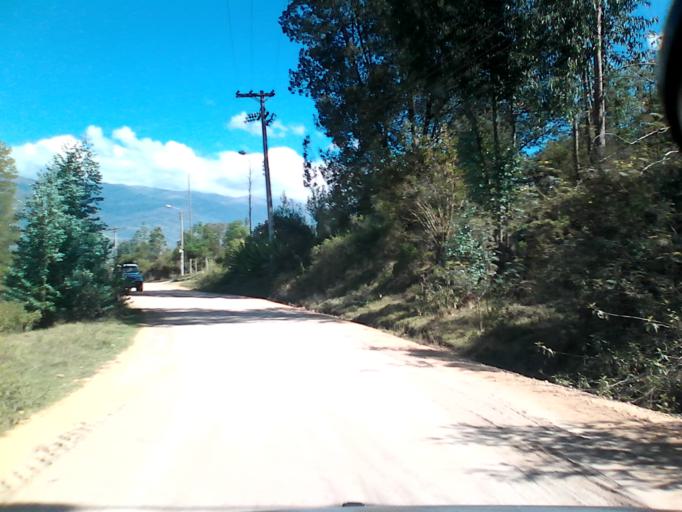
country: CO
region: Boyaca
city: Duitama
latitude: 5.7924
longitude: -73.0138
